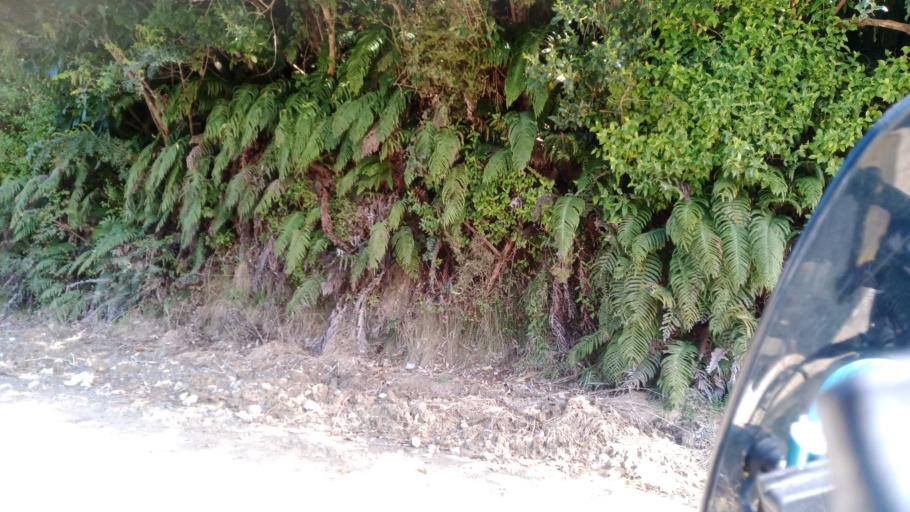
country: NZ
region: Gisborne
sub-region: Gisborne District
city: Gisborne
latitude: -38.8755
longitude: 177.7869
